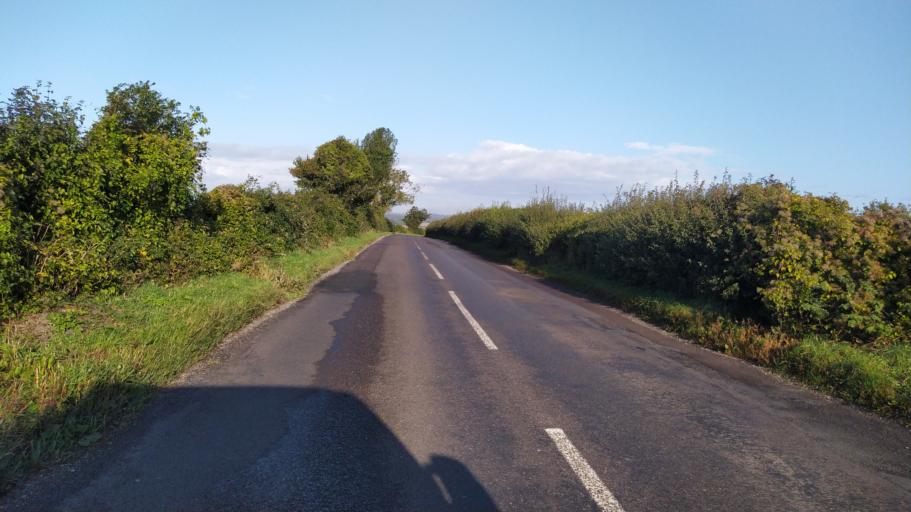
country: GB
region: England
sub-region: Wiltshire
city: Bower Chalke
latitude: 50.9098
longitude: -2.0426
